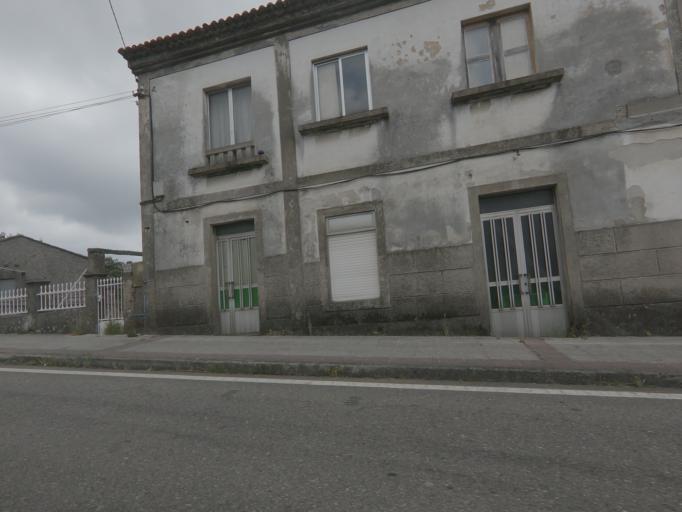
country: ES
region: Galicia
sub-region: Provincia de Pontevedra
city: O Rosal
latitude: 41.9265
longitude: -8.8048
